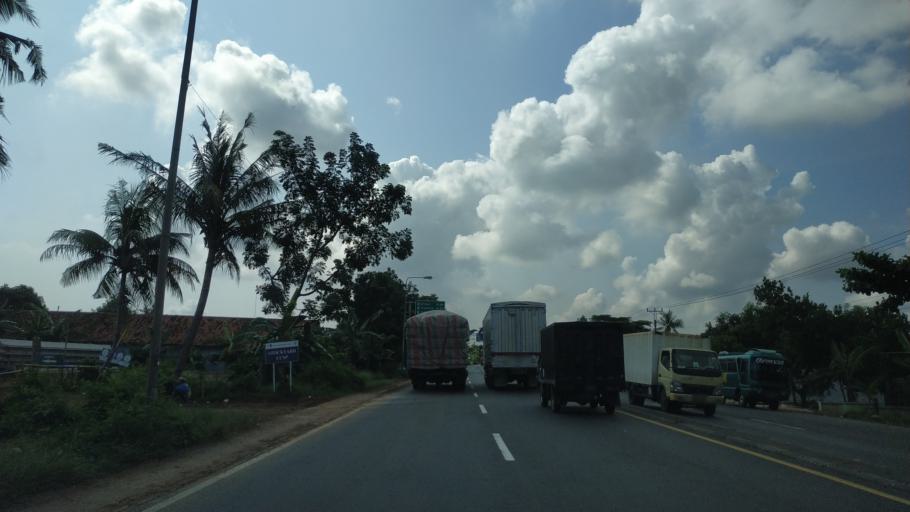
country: ID
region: Central Java
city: Comal
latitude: -6.8860
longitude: 109.5710
